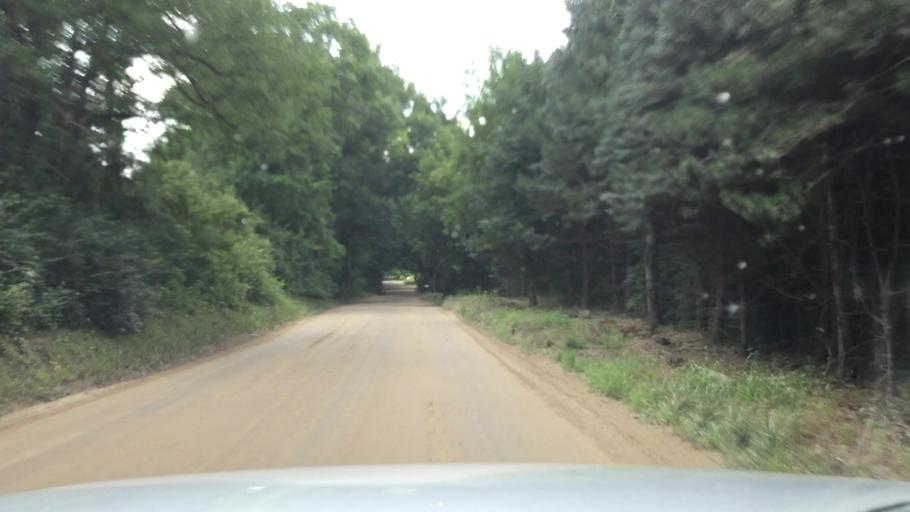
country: US
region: Michigan
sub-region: Ionia County
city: Belding
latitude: 43.1228
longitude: -85.2135
